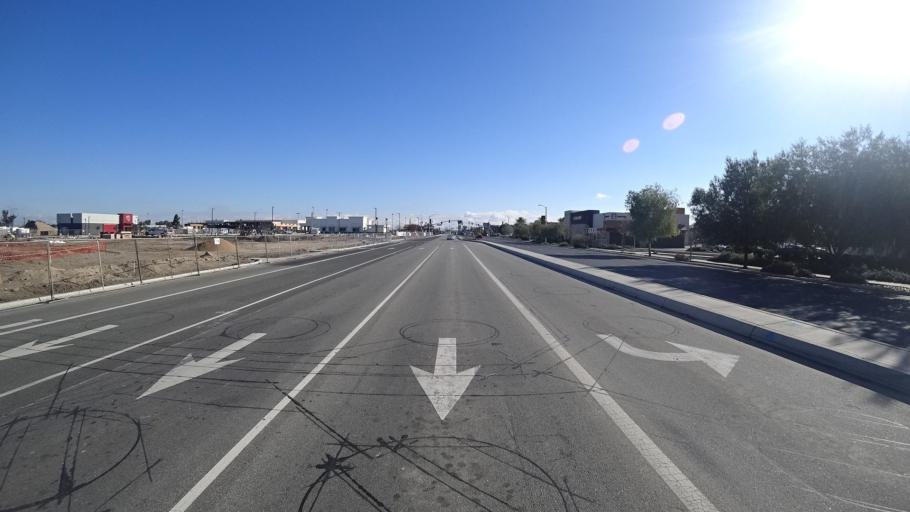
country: US
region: California
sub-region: Kern County
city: Delano
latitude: 35.7469
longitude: -119.2493
